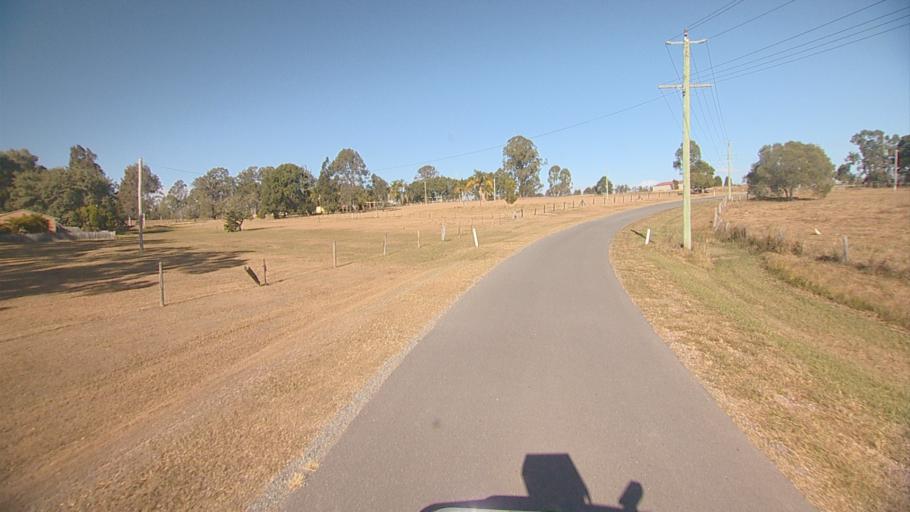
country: AU
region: Queensland
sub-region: Logan
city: Cedar Vale
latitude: -27.8494
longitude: 153.0086
